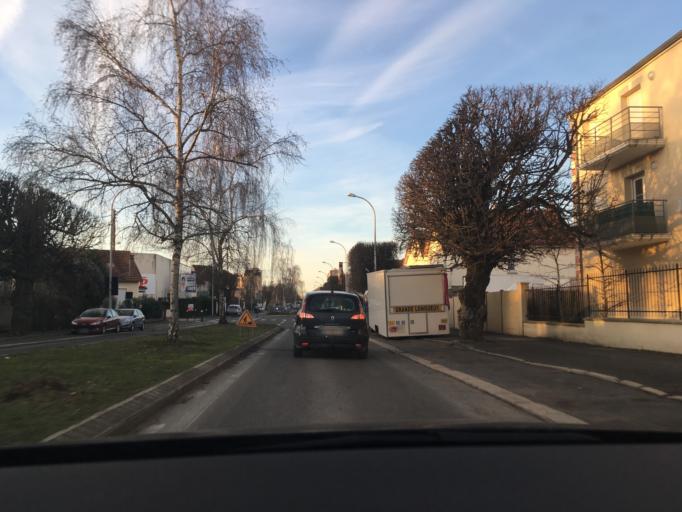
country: FR
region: Ile-de-France
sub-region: Departement de Seine-et-Marne
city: Melun
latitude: 48.5476
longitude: 2.6514
